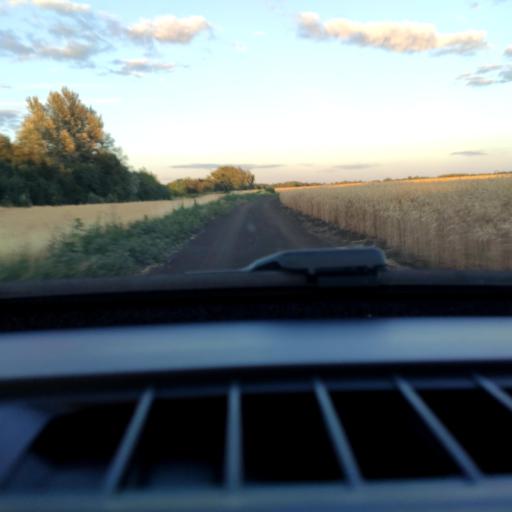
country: RU
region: Voronezj
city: Verkhnyaya Khava
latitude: 51.5907
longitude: 39.8603
